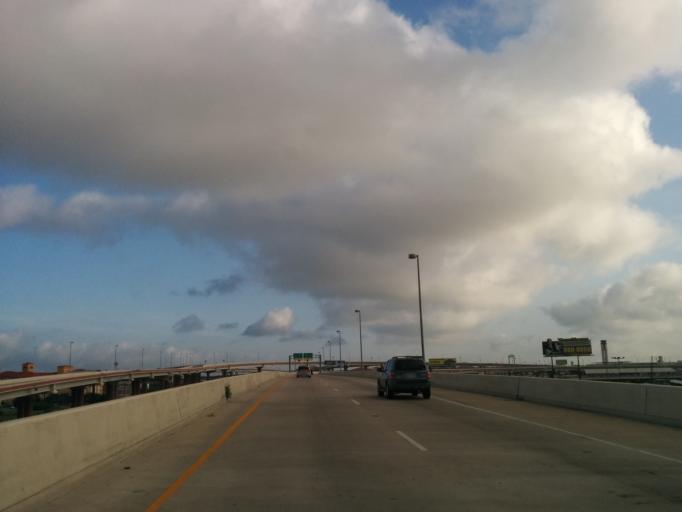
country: US
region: Texas
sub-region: Bexar County
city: Alamo Heights
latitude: 29.5146
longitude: -98.4768
